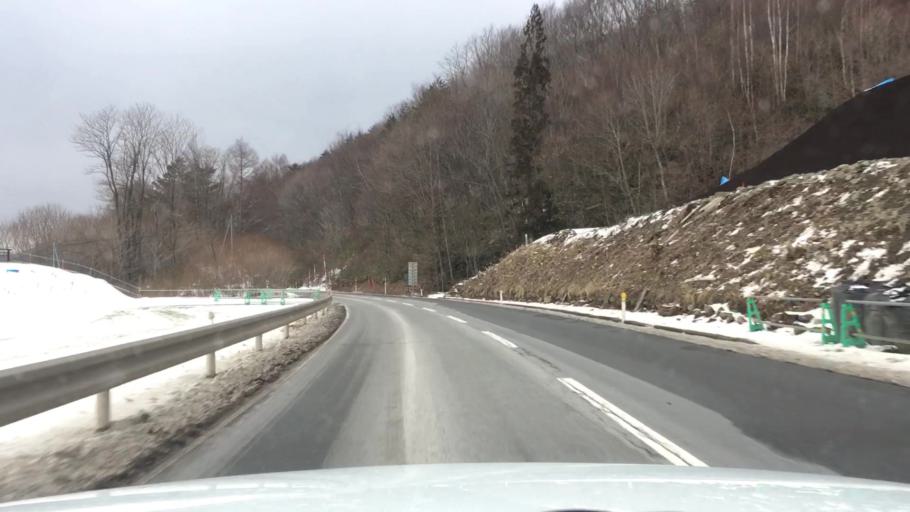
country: JP
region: Iwate
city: Morioka-shi
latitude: 39.6360
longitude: 141.4379
